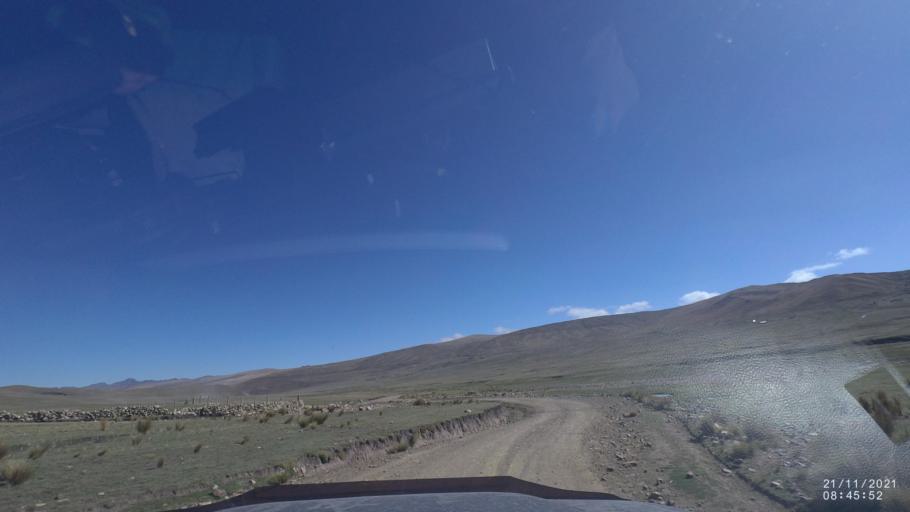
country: BO
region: Cochabamba
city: Cochabamba
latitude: -17.2457
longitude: -66.2322
